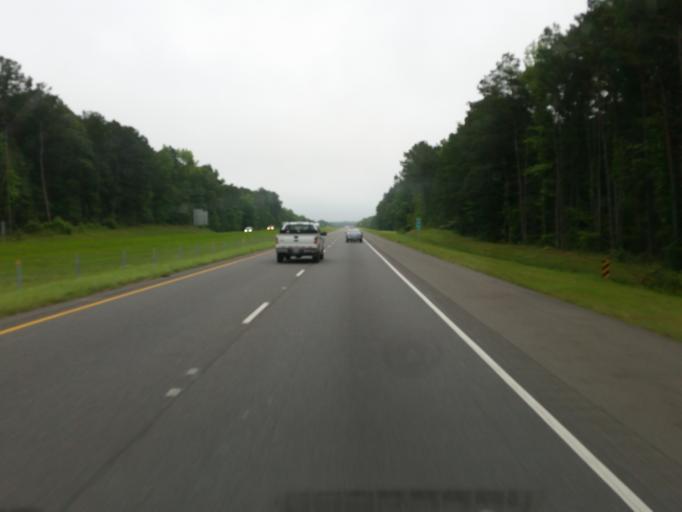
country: US
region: Louisiana
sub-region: Bossier Parish
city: Haughton
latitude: 32.5608
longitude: -93.4994
